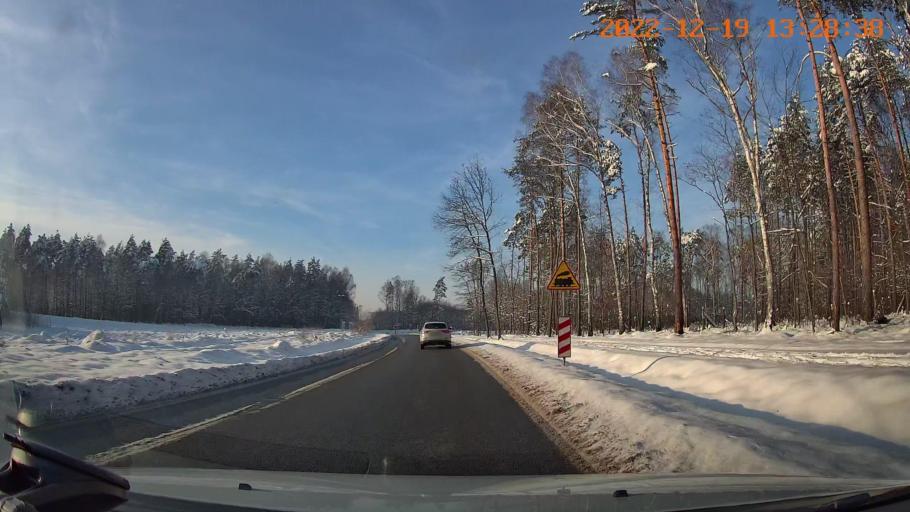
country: PL
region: Silesian Voivodeship
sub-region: Powiat bierunsko-ledzinski
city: Ledziny
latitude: 50.1128
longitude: 19.1260
